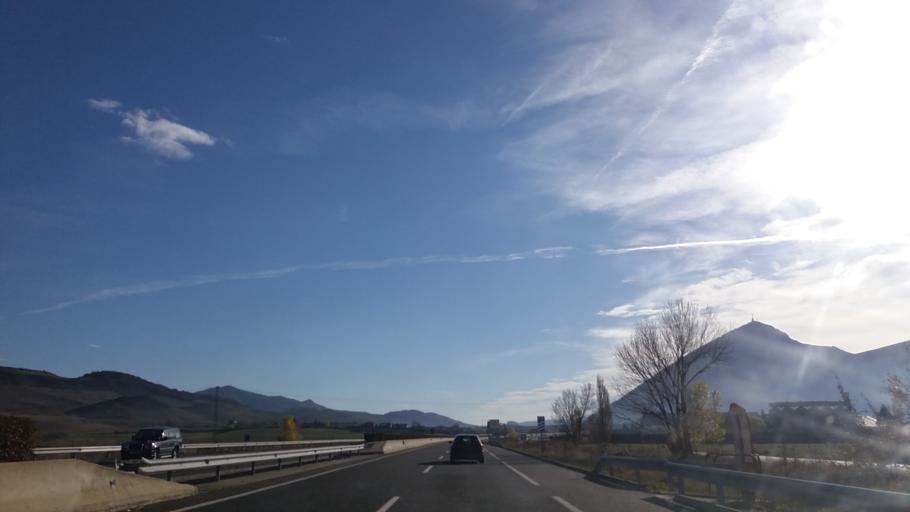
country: ES
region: Navarre
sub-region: Provincia de Navarra
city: Elorz
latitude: 42.7366
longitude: -1.5748
